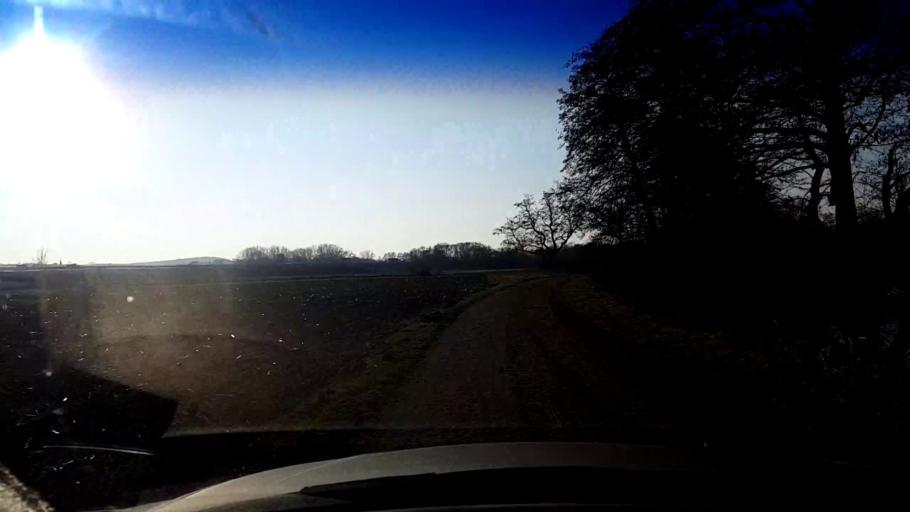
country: DE
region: Bavaria
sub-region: Upper Franconia
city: Bischberg
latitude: 49.9187
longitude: 10.8528
